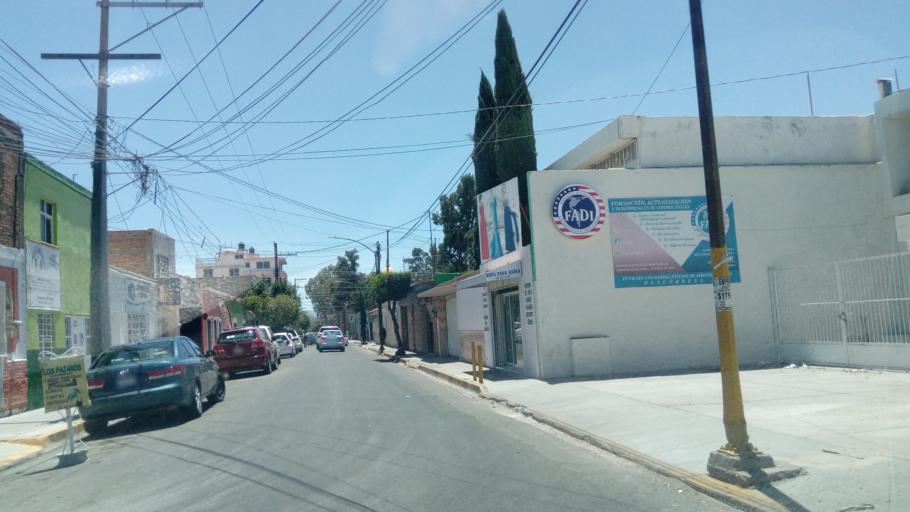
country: MX
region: Durango
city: Victoria de Durango
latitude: 24.0290
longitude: -104.6617
